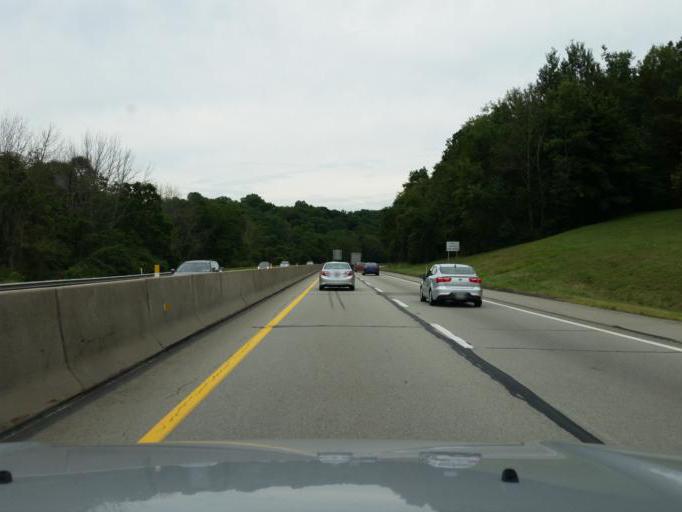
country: US
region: Pennsylvania
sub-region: Westmoreland County
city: Level Green
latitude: 40.4289
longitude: -79.7416
